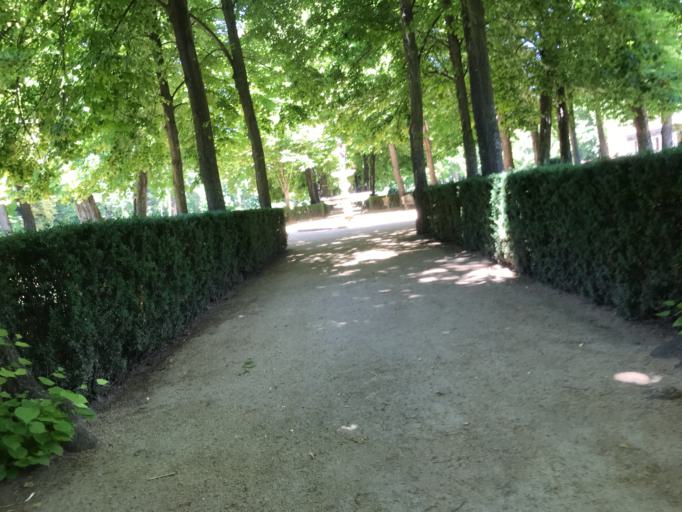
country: ES
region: Madrid
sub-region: Provincia de Madrid
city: Aranjuez
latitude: 40.0390
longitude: -3.6106
